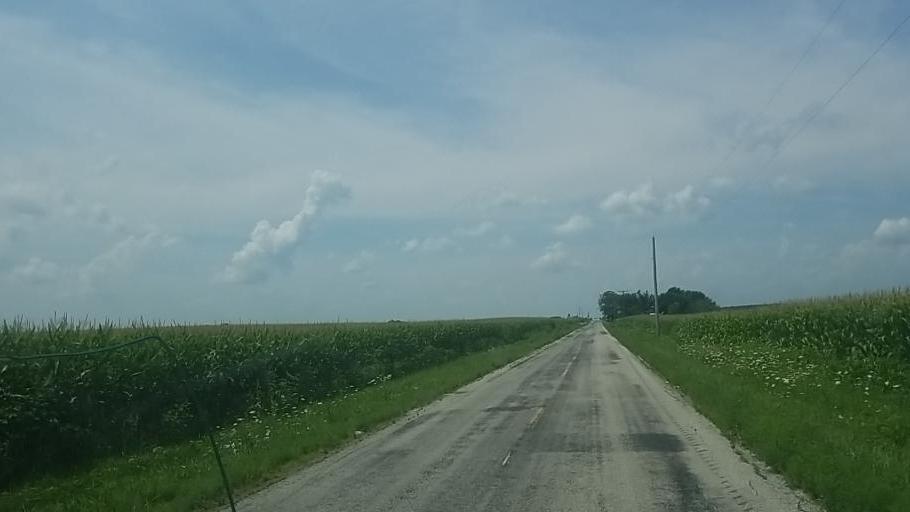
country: US
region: Ohio
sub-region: Marion County
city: Marion
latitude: 40.6734
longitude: -83.1970
